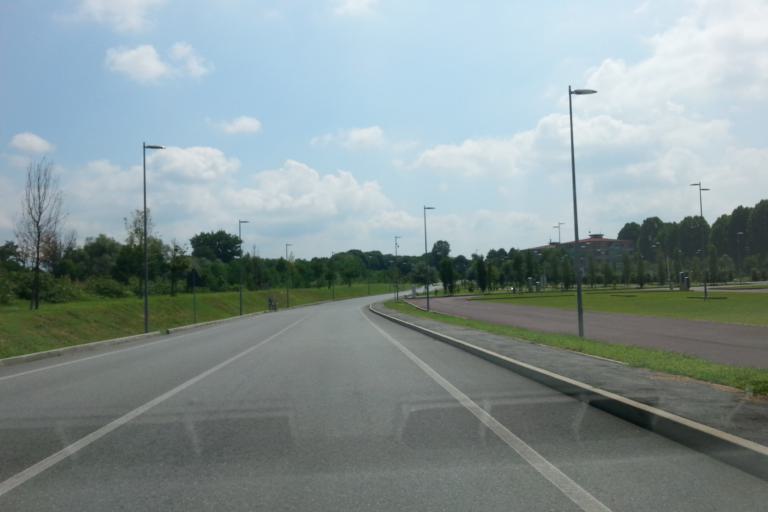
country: IT
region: Piedmont
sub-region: Provincia di Torino
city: Venaria Reale
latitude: 45.1396
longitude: 7.6231
